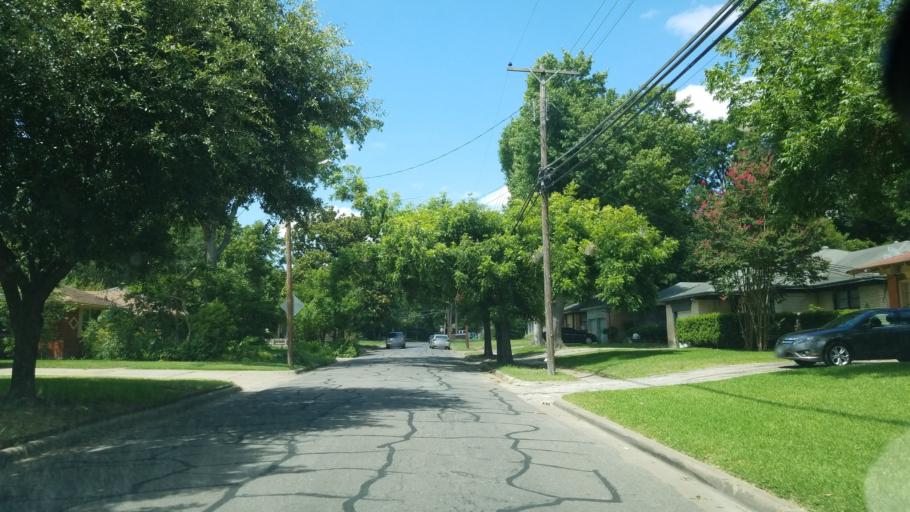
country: US
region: Texas
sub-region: Dallas County
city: Balch Springs
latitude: 32.7589
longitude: -96.6998
